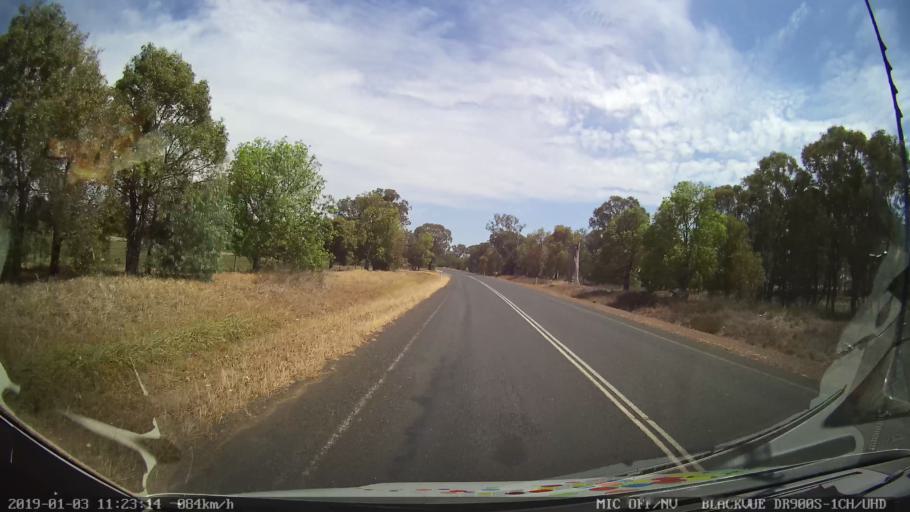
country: AU
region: New South Wales
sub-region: Weddin
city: Grenfell
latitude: -34.0655
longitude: 148.2437
